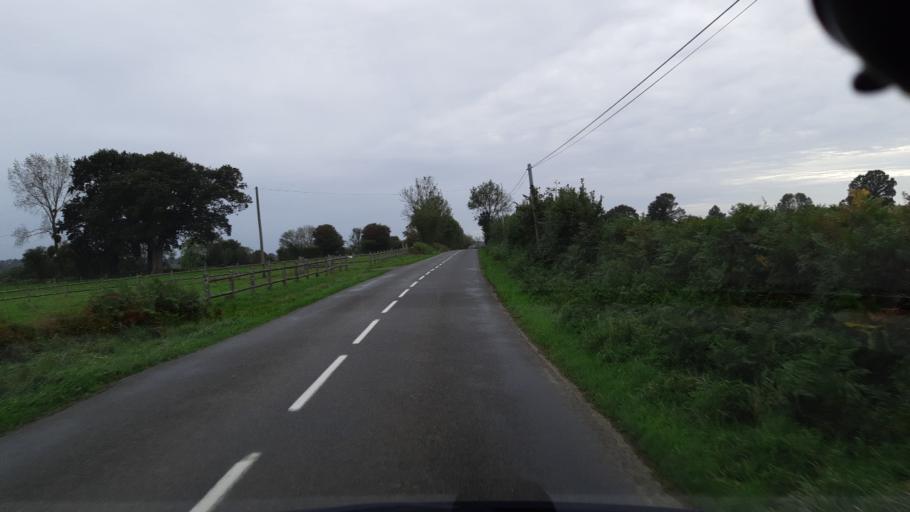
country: FR
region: Lower Normandy
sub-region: Departement de la Manche
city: Hambye
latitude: 48.9659
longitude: -1.2602
